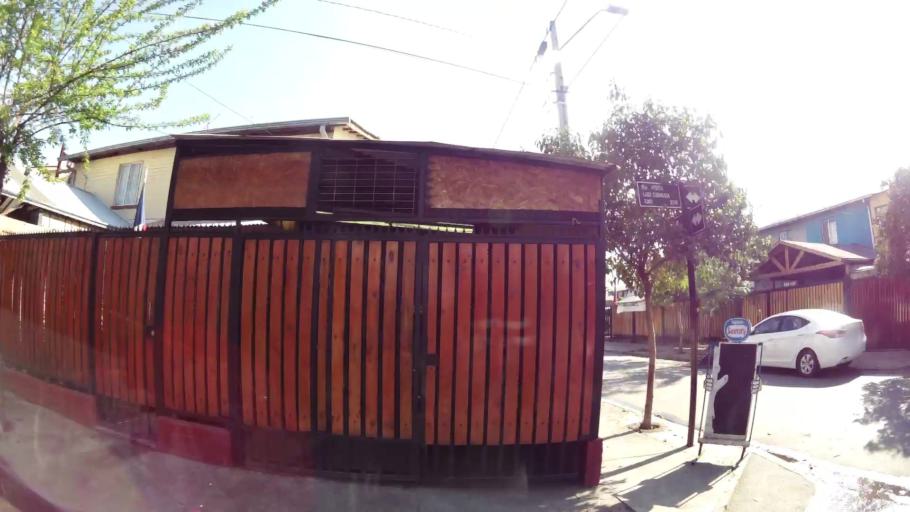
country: CL
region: Santiago Metropolitan
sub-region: Provincia de Santiago
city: La Pintana
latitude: -33.5629
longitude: -70.6325
